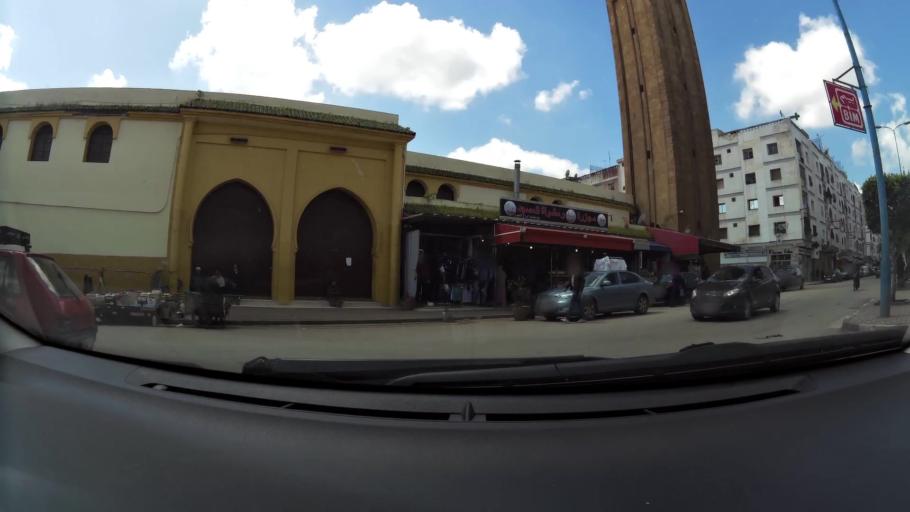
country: MA
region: Grand Casablanca
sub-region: Mediouna
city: Tit Mellil
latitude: 33.5384
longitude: -7.5547
